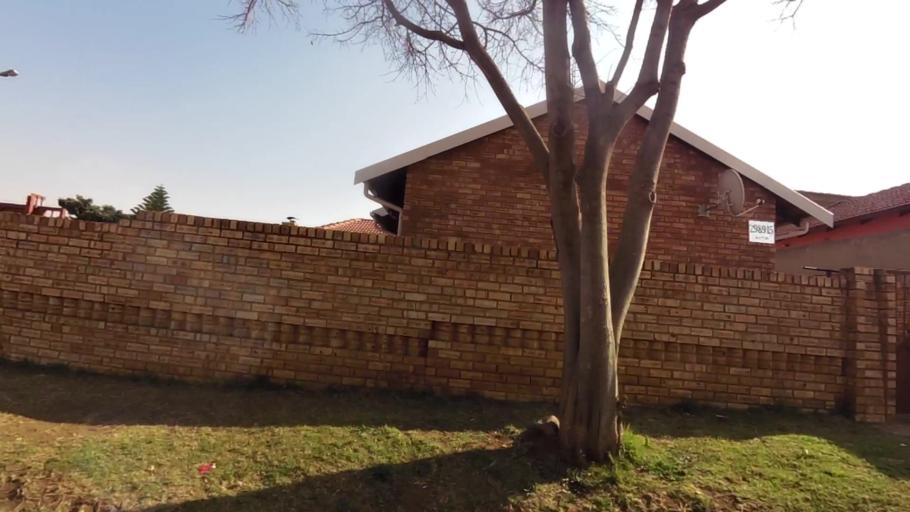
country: ZA
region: Gauteng
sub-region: City of Johannesburg Metropolitan Municipality
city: Soweto
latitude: -26.2892
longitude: 27.9515
